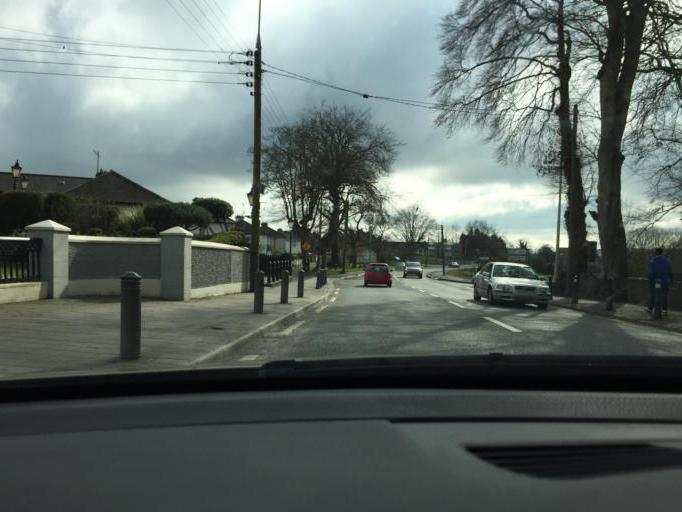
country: IE
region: Leinster
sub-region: Wicklow
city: Blessington
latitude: 53.1692
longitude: -6.5346
